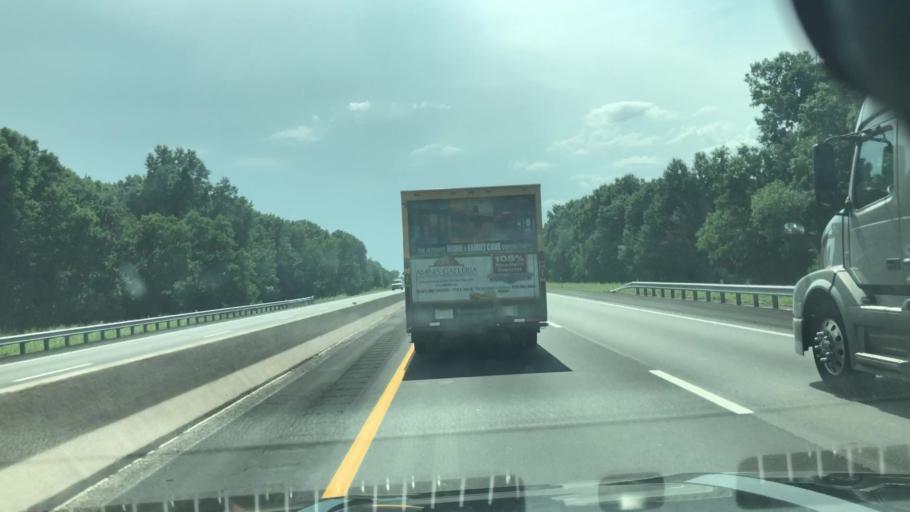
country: US
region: Oklahoma
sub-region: Craig County
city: Vinita
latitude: 36.6615
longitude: -95.0895
